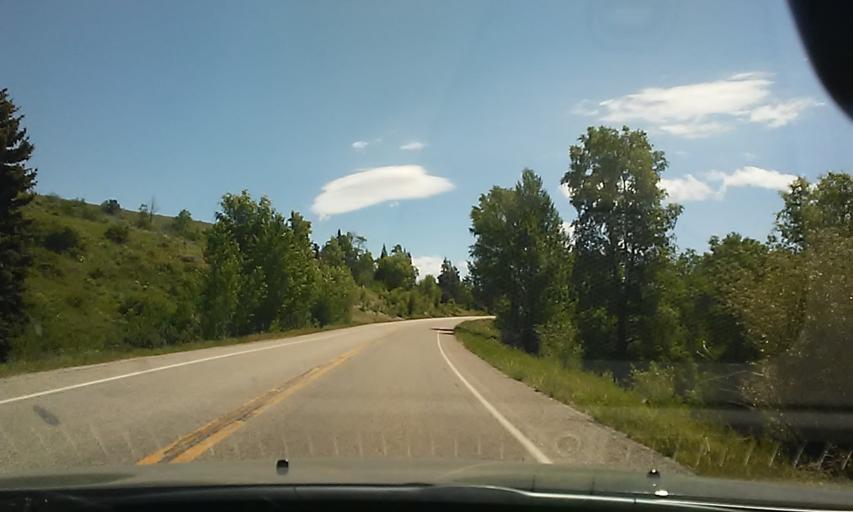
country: US
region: Wyoming
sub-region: Teton County
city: Jackson
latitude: 43.8392
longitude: -110.4898
